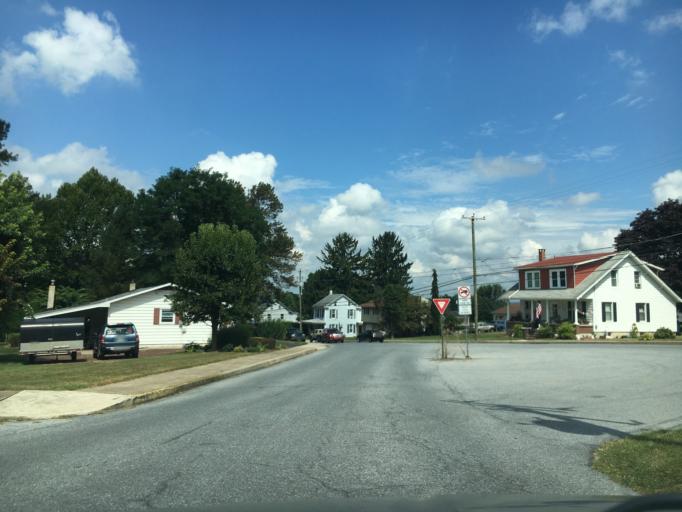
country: US
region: Pennsylvania
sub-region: Berks County
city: Fleetwood
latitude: 40.4489
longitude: -75.8142
